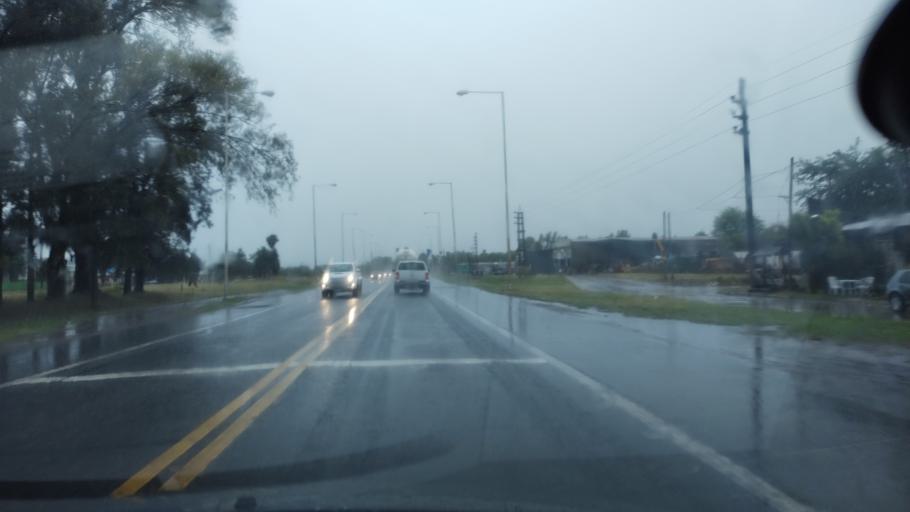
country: AR
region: Buenos Aires
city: Canuelas
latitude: -35.0435
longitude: -58.7644
